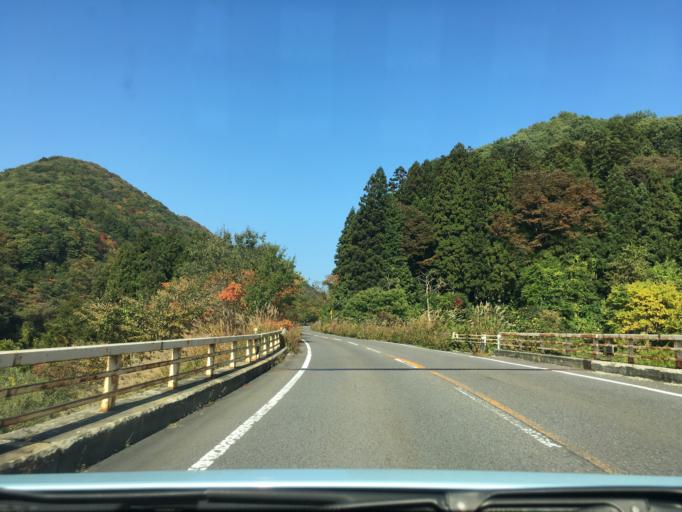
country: JP
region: Fukushima
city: Sukagawa
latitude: 37.3157
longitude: 140.1385
